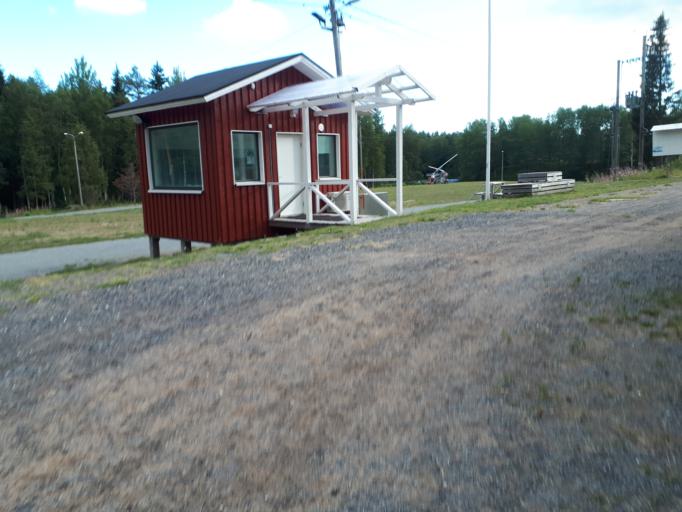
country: FI
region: Northern Ostrobothnia
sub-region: Oulunkaari
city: Ii
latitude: 65.3309
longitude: 25.3895
